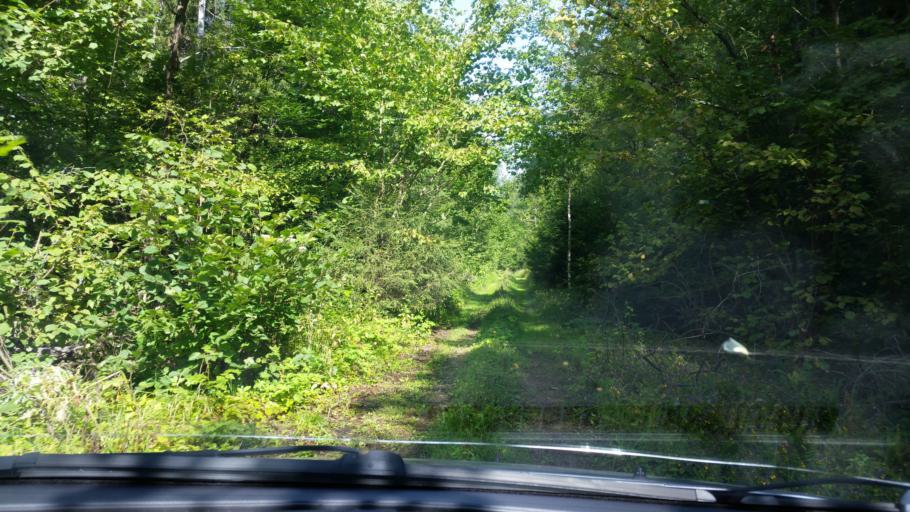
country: RU
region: Moskovskaya
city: Bol'shoye Gryzlovo
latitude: 54.9127
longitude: 37.7547
